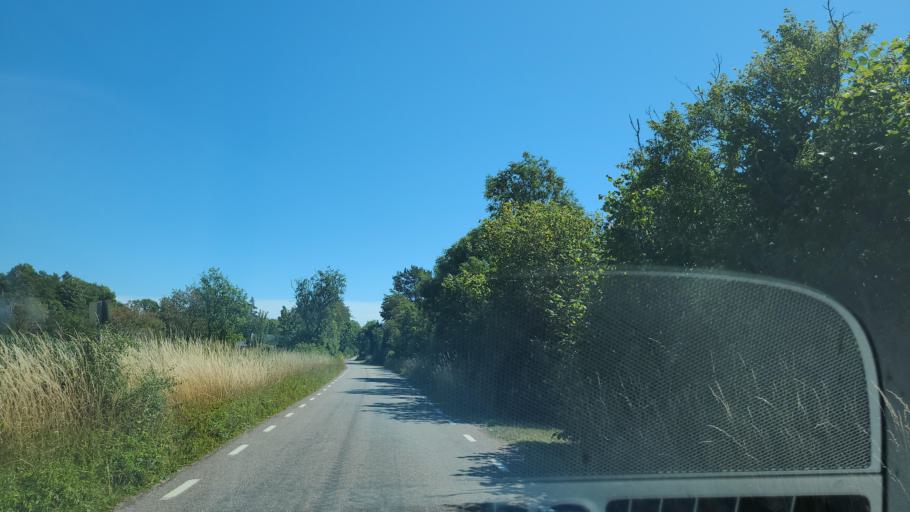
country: SE
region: Kalmar
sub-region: Borgholms Kommun
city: Borgholm
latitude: 56.7468
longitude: 16.6883
